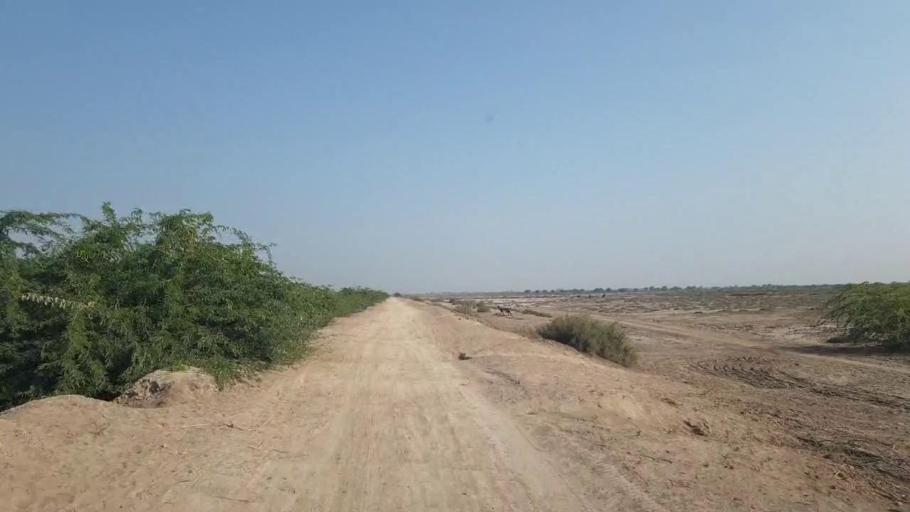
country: PK
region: Sindh
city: Badin
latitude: 24.4701
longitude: 68.7406
